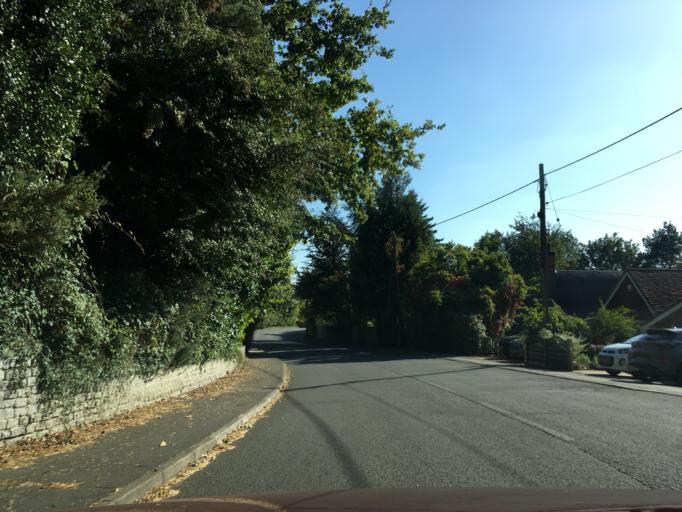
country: GB
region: England
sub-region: West Berkshire
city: Cold Ash
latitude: 51.4248
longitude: -1.2649
